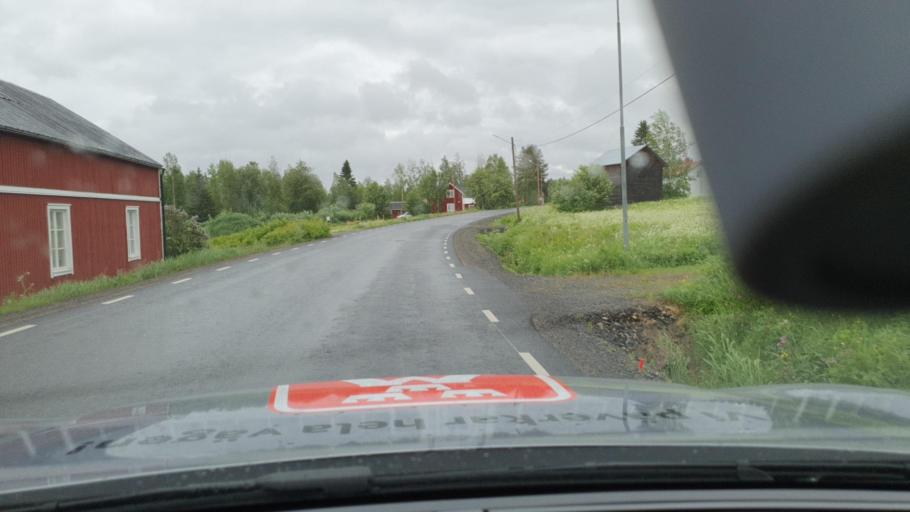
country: FI
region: Lapland
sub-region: Torniolaakso
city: Ylitornio
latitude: 66.1976
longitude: 23.7122
